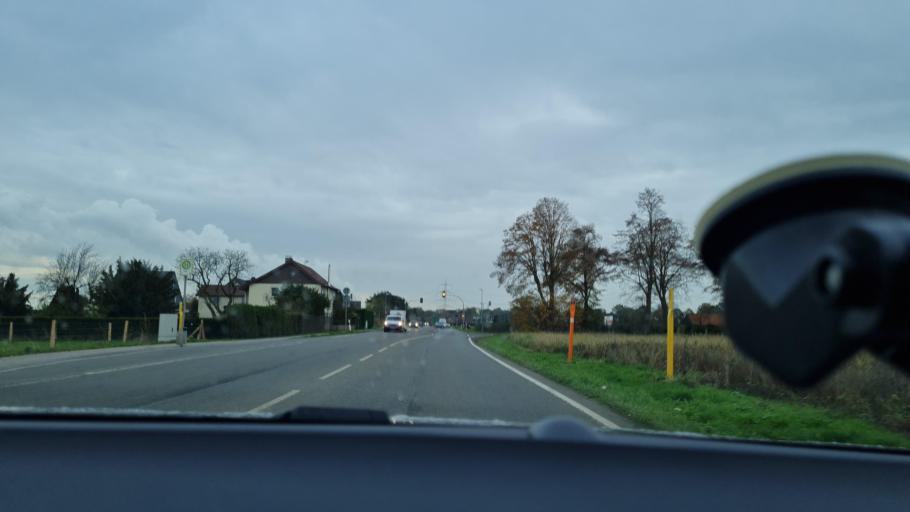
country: DE
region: North Rhine-Westphalia
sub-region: Regierungsbezirk Dusseldorf
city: Voerde
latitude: 51.6107
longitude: 6.6514
